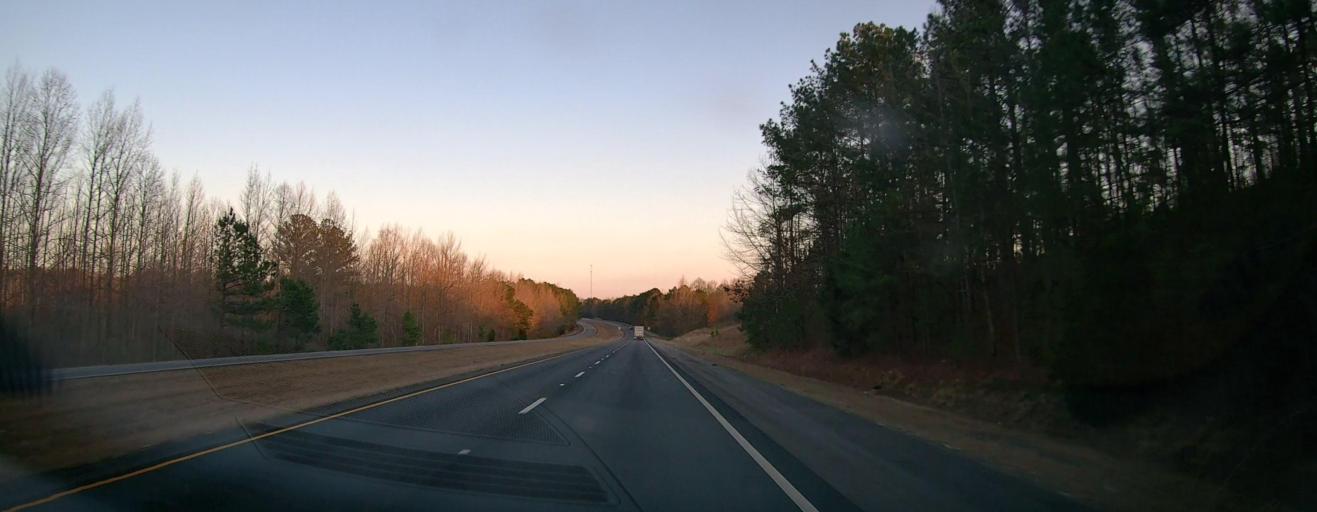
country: US
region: Alabama
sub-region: Coosa County
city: Goodwater
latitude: 33.0528
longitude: -86.1440
